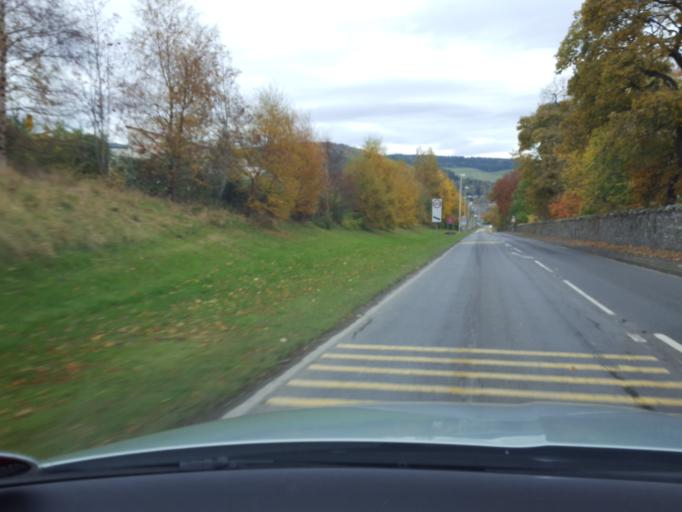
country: GB
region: Scotland
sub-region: The Scottish Borders
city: Peebles
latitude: 55.6527
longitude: -3.2080
